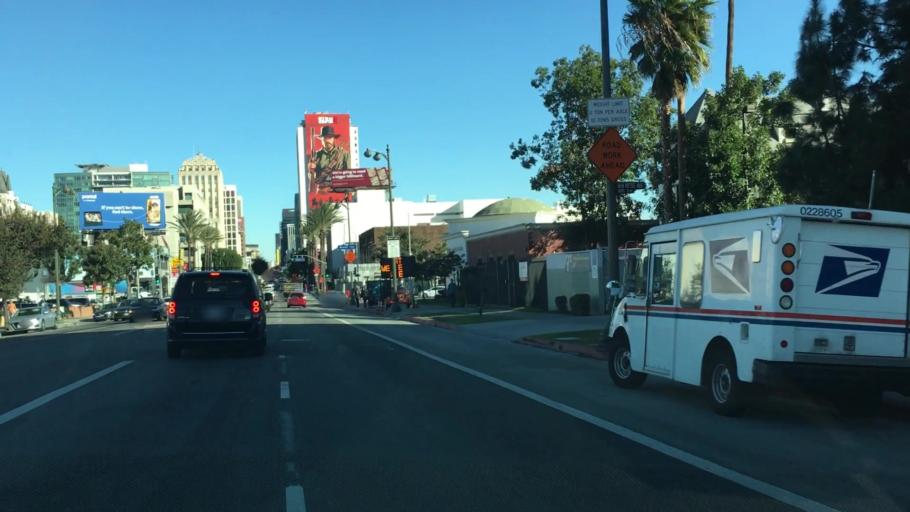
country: US
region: California
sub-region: Los Angeles County
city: Hollywood
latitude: 34.0617
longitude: -118.3154
